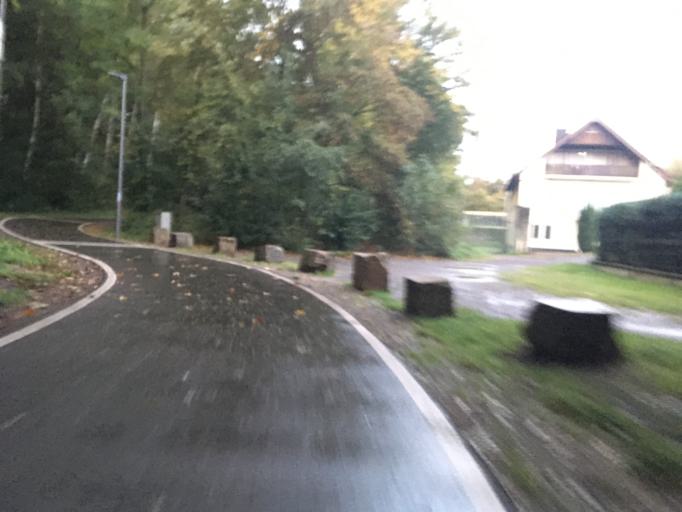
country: DE
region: North Rhine-Westphalia
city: Hattingen
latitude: 51.4355
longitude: 7.1676
